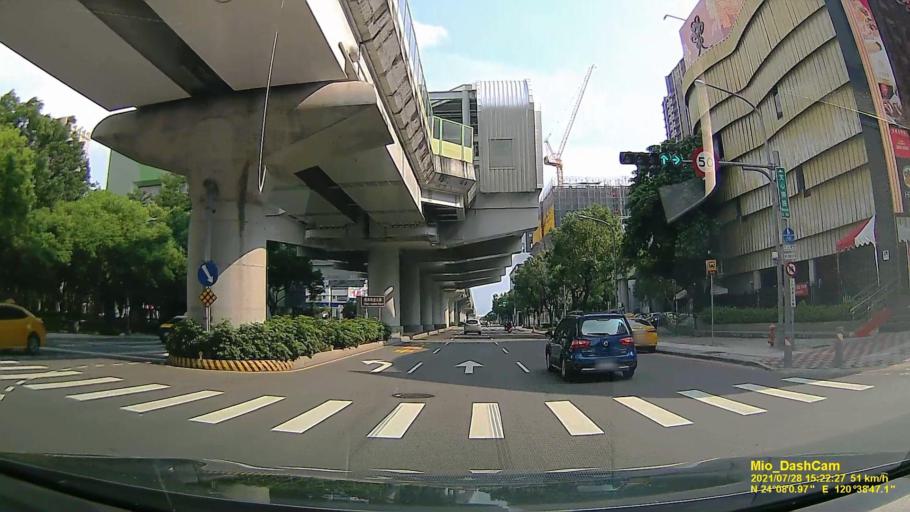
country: TW
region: Taiwan
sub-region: Taichung City
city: Taichung
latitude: 24.1335
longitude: 120.6464
